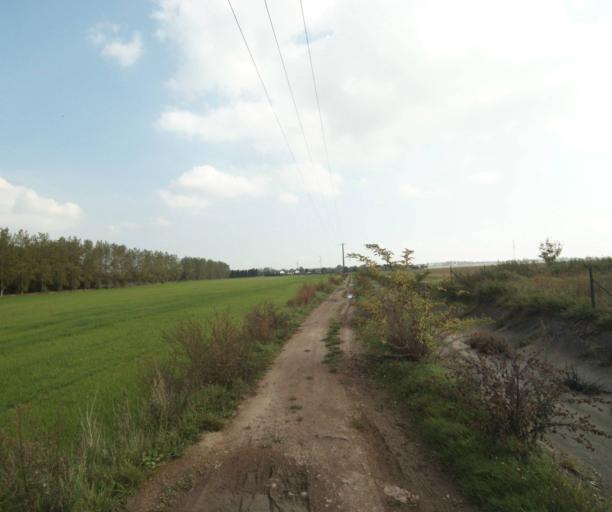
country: FR
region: Nord-Pas-de-Calais
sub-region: Departement du Nord
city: Emmerin
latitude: 50.5791
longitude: 3.0029
